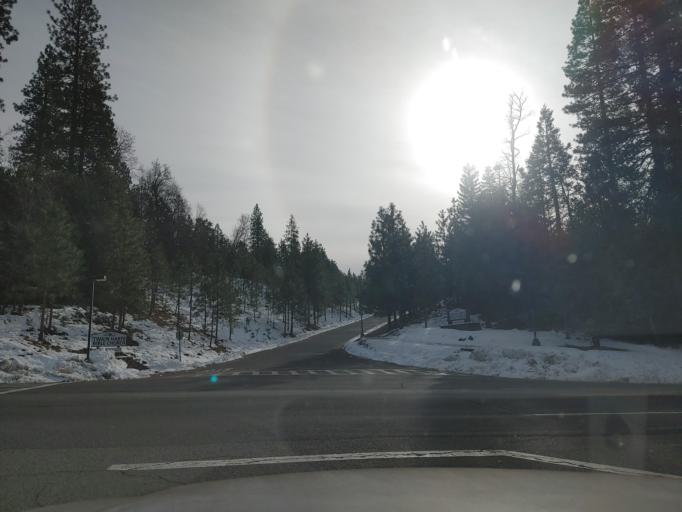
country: US
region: California
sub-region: Tuolumne County
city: Twain Harte
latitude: 38.0402
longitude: -120.2216
